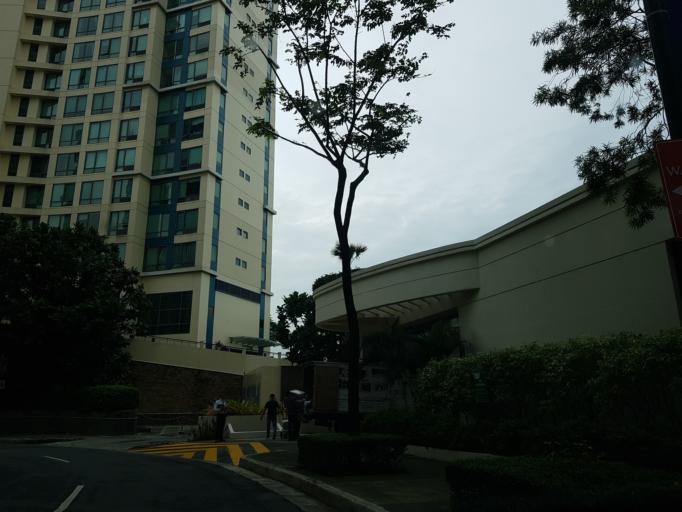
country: PH
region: Metro Manila
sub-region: Makati City
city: Makati City
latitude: 14.5532
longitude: 121.0437
